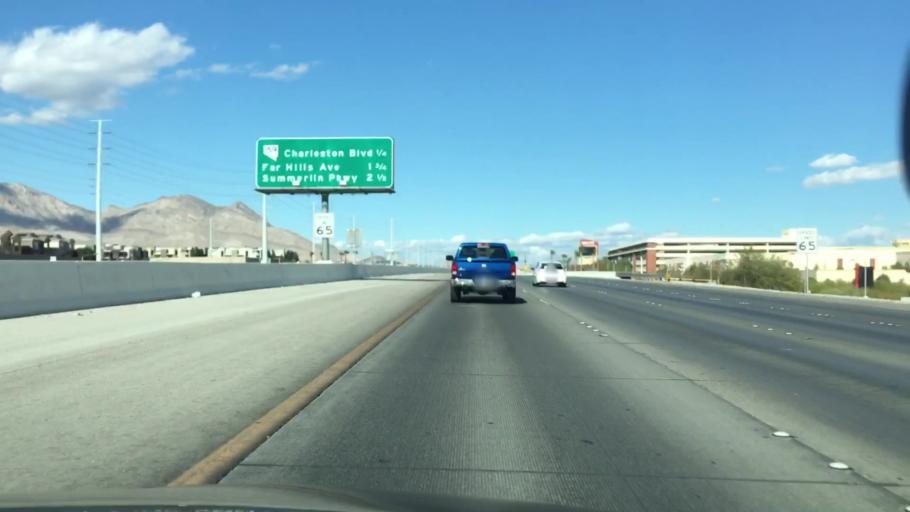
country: US
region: Nevada
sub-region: Clark County
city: Summerlin South
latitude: 36.1515
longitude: -115.3368
